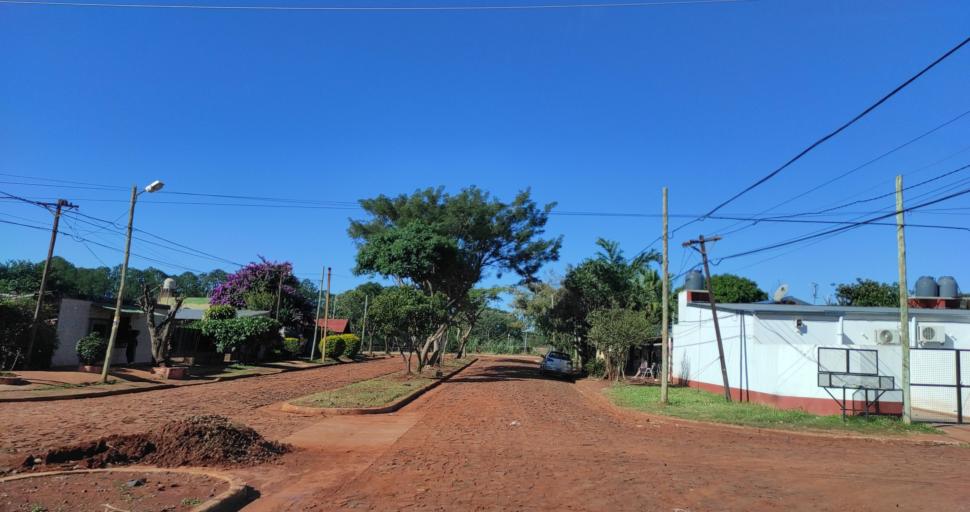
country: AR
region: Misiones
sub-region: Departamento de Capital
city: Posadas
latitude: -27.4273
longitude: -55.9315
